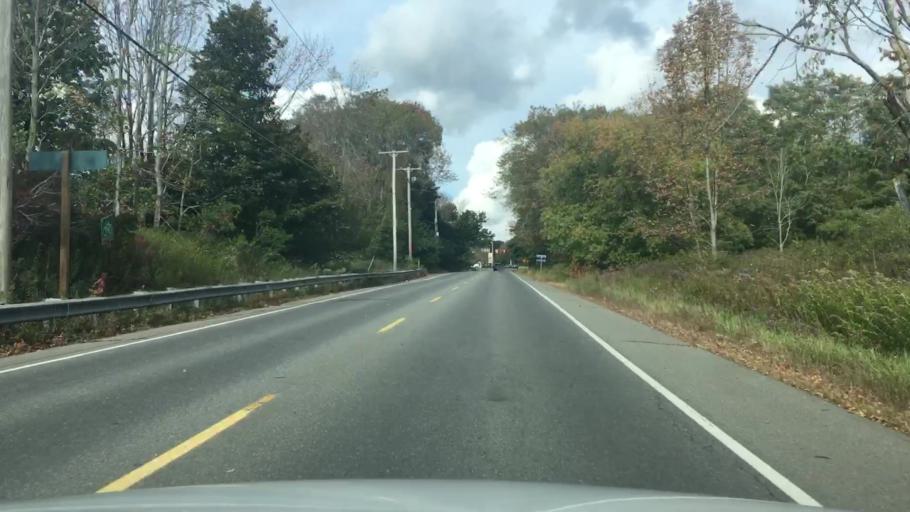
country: US
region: Maine
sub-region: Knox County
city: Rockland
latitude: 44.1218
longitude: -69.1147
